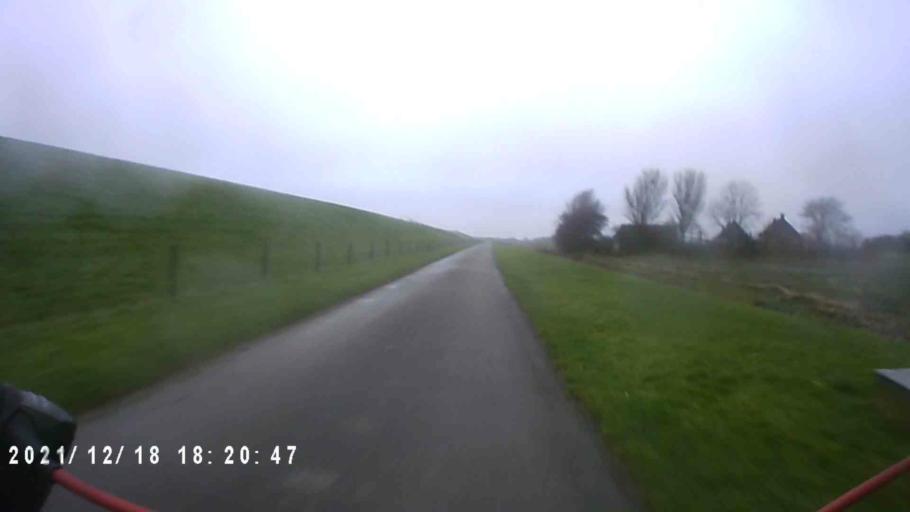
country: NL
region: Friesland
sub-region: Gemeente Dongeradeel
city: Ternaard
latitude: 53.3951
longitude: 5.9832
